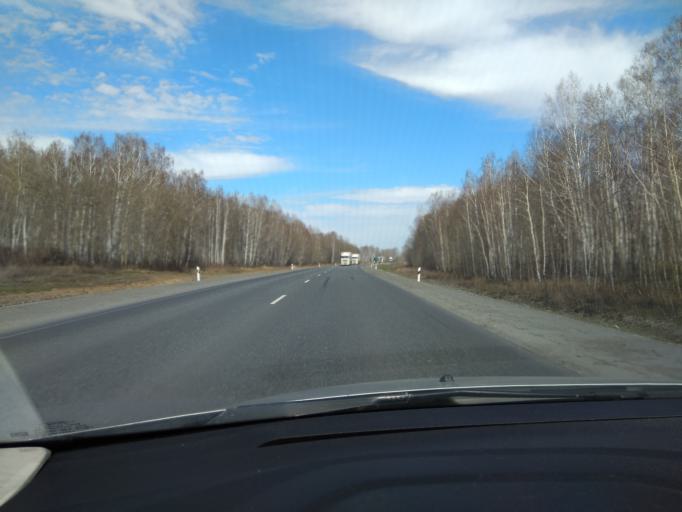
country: RU
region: Sverdlovsk
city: Pyshma
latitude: 56.9279
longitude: 63.1549
